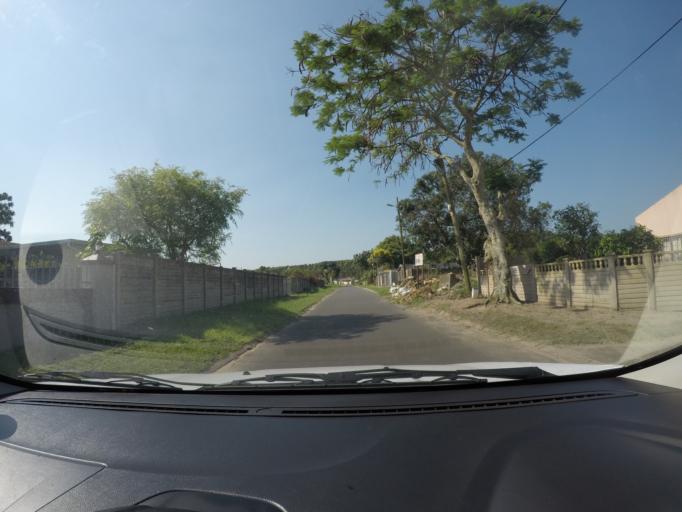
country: ZA
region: KwaZulu-Natal
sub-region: uThungulu District Municipality
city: Richards Bay
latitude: -28.7173
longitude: 32.0445
